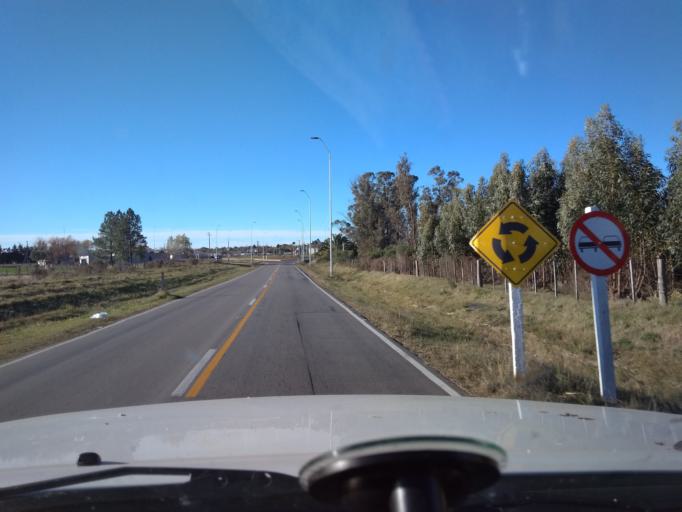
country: UY
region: Canelones
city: Santa Rosa
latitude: -34.5067
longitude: -56.0505
